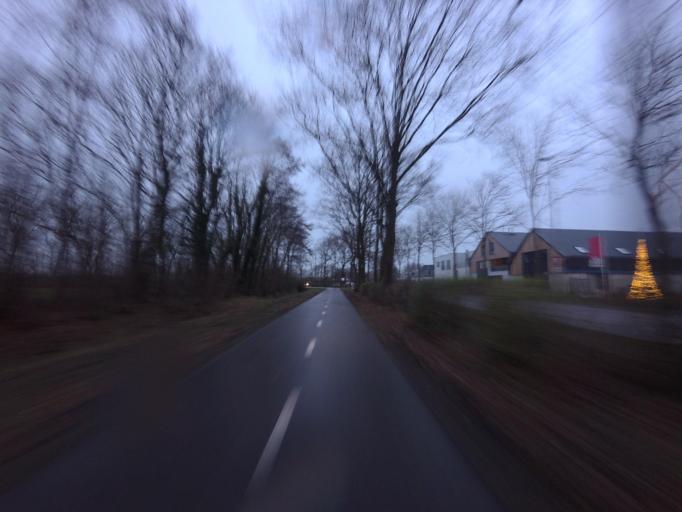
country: NL
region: North Holland
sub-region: Gemeente Texel
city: Den Burg
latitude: 53.0617
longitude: 4.8008
